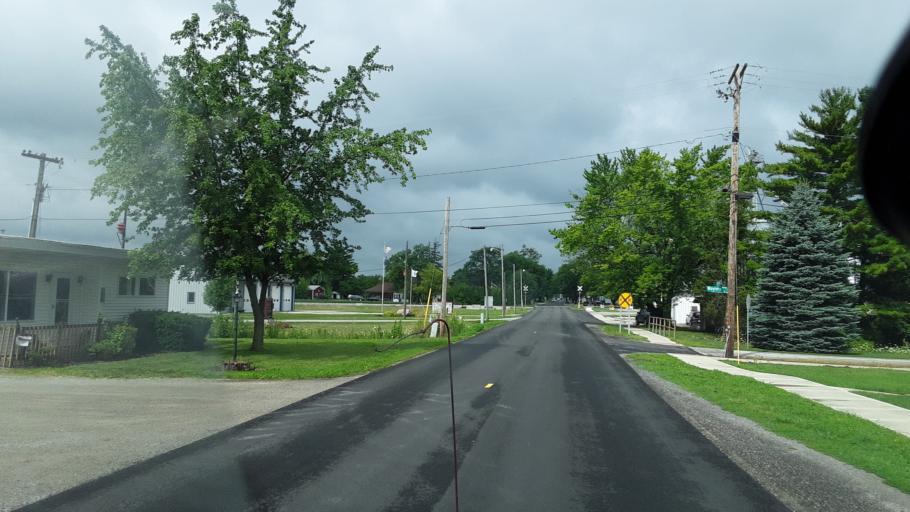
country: US
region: Indiana
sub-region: Allen County
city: Monroeville
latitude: 40.9482
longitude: -84.9895
